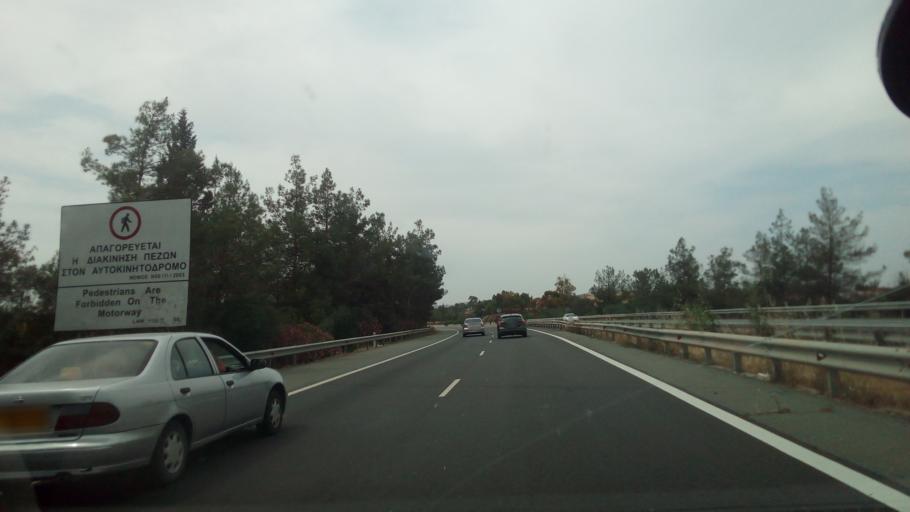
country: CY
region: Larnaka
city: Aradippou
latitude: 34.9601
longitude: 33.5697
